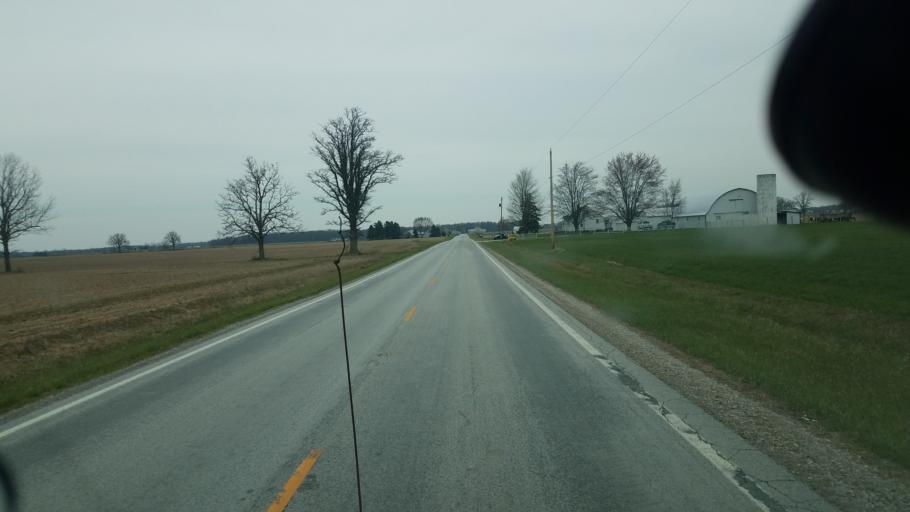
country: US
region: Ohio
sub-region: Hardin County
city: Forest
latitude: 40.8805
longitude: -83.5247
